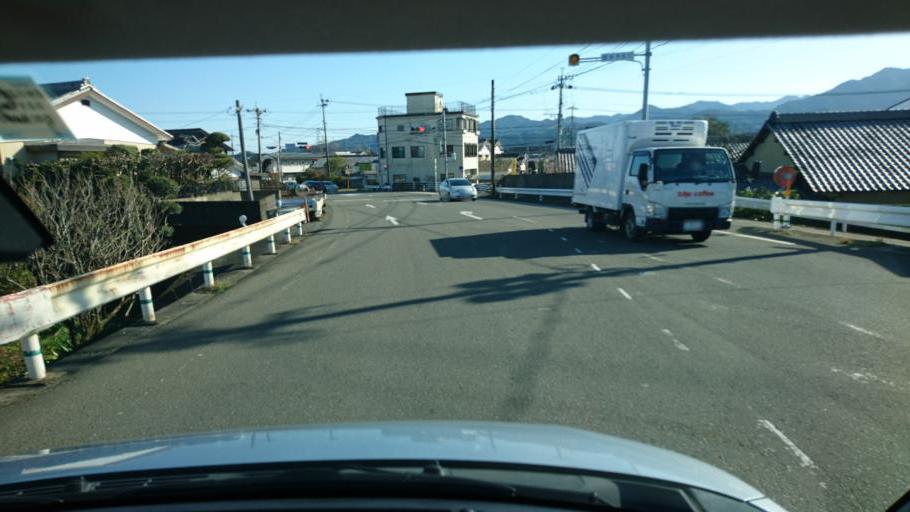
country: JP
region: Miyazaki
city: Miyazaki-shi
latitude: 31.8339
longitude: 131.4376
